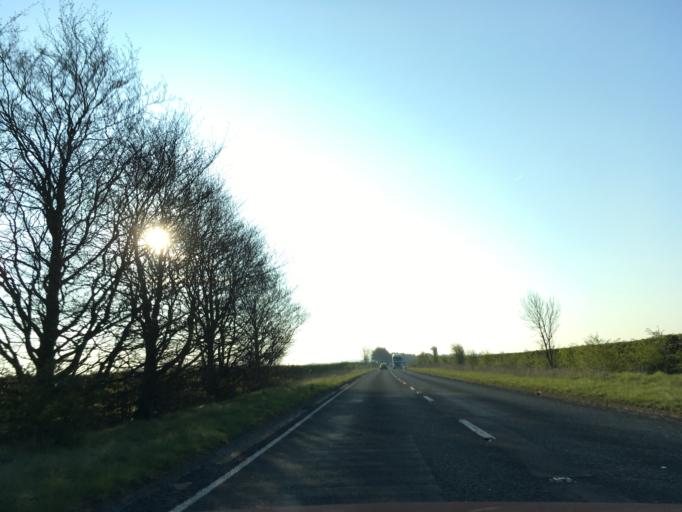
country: GB
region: England
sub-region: Gloucestershire
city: Northleach
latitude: 51.8430
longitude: -1.8517
